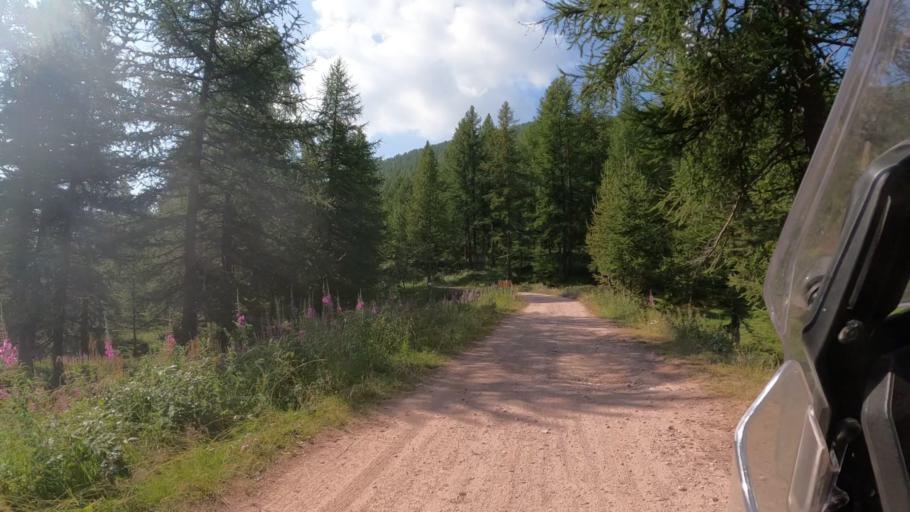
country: IT
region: Piedmont
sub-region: Provincia di Cuneo
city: Briga Alta
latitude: 44.1099
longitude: 7.7033
